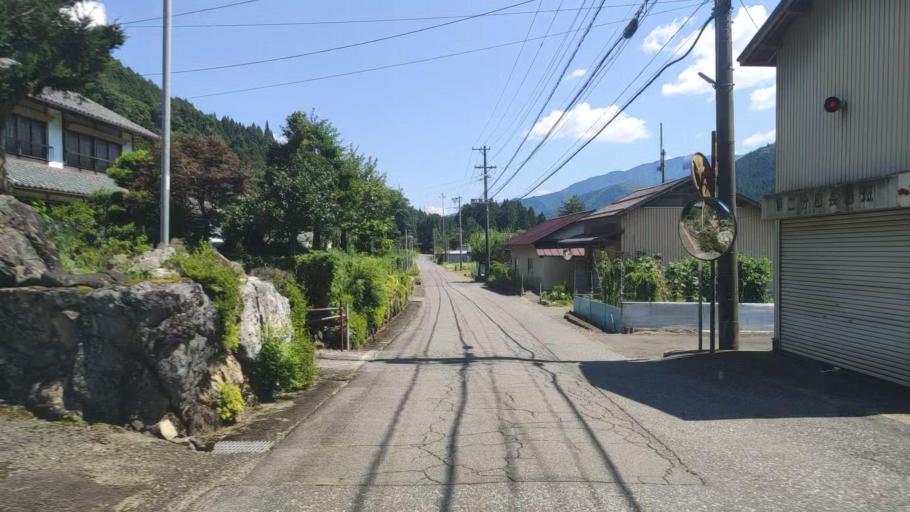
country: JP
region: Gifu
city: Godo
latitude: 35.6782
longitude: 136.5724
